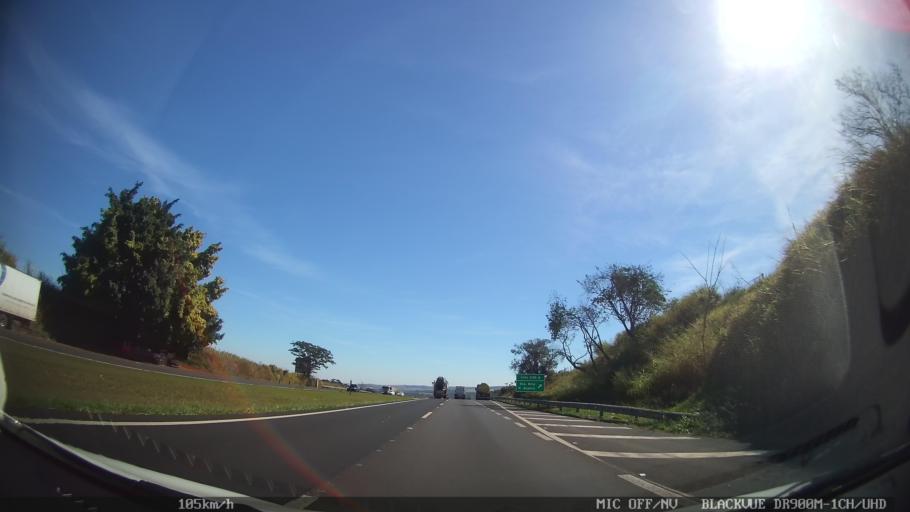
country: BR
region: Sao Paulo
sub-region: Santa Rita Do Passa Quatro
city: Santa Rita do Passa Quatro
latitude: -21.7589
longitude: -47.5600
